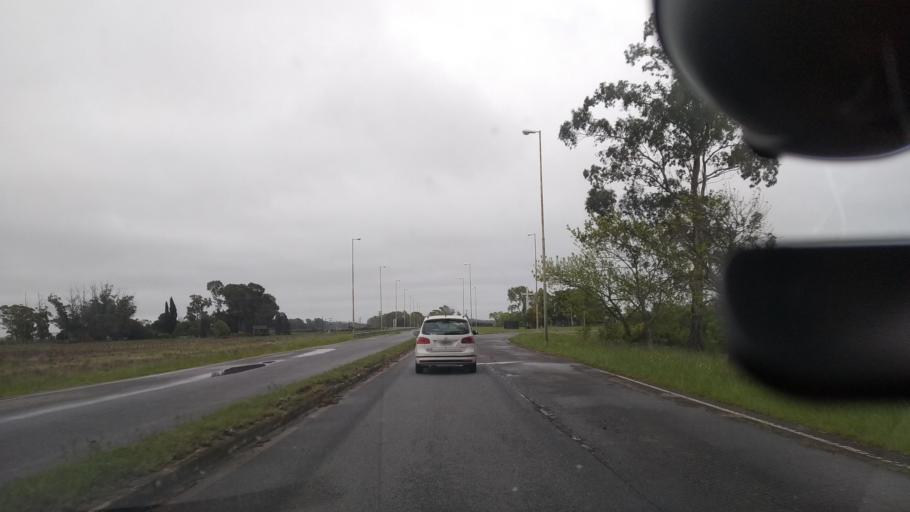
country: AR
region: Buenos Aires
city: Veronica
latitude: -35.3849
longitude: -57.3647
